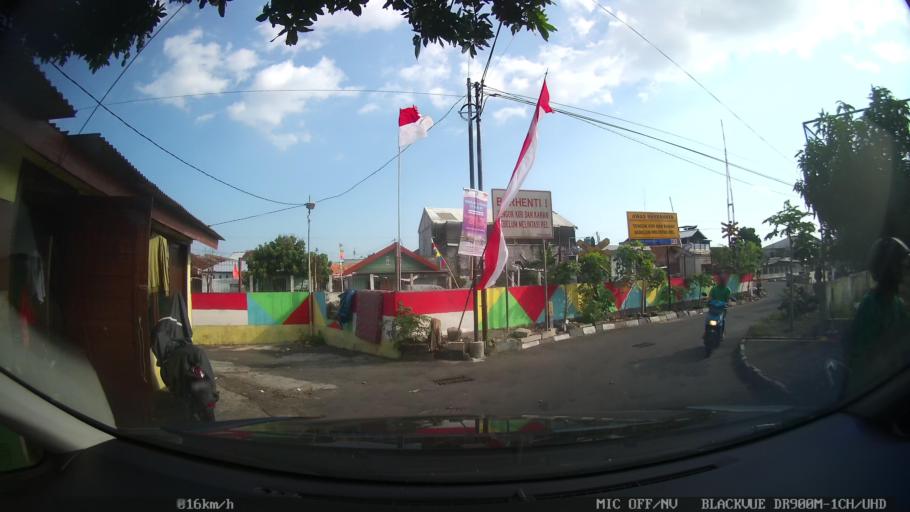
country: ID
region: Daerah Istimewa Yogyakarta
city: Yogyakarta
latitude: -7.7881
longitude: 110.3516
